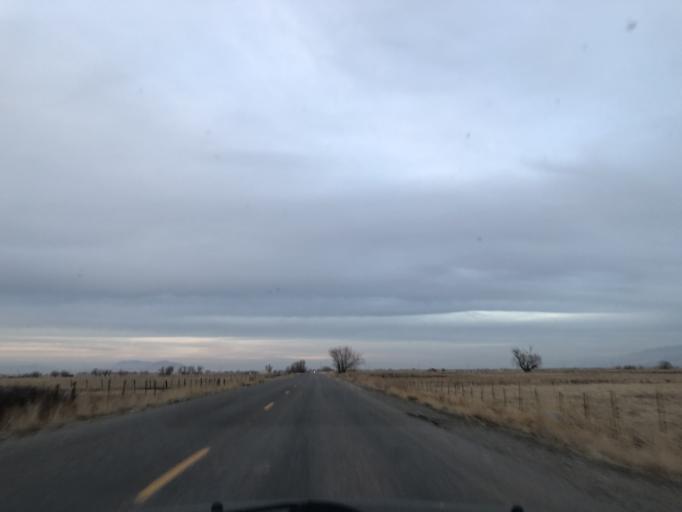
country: US
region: Utah
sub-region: Cache County
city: Benson
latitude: 41.7537
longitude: -111.9116
